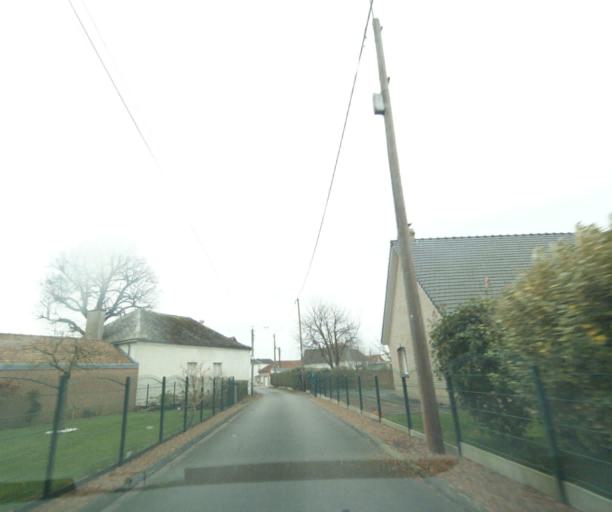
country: FR
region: Nord-Pas-de-Calais
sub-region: Departement du Nord
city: Quarouble
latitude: 50.3865
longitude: 3.6308
